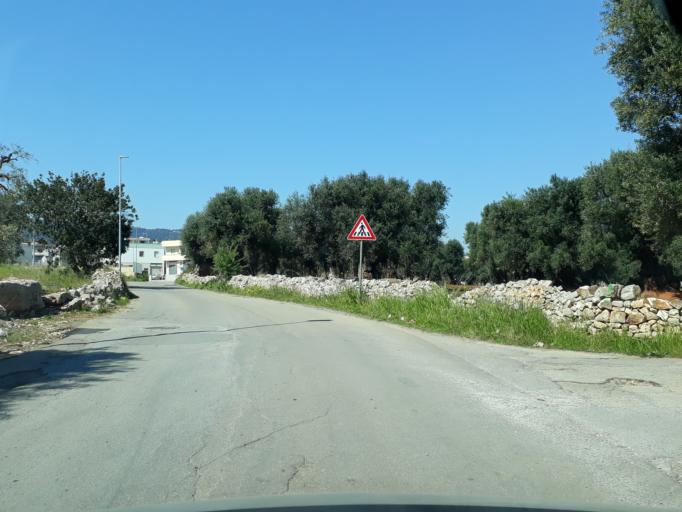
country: IT
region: Apulia
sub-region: Provincia di Brindisi
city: Fasano
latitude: 40.8359
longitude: 17.3687
